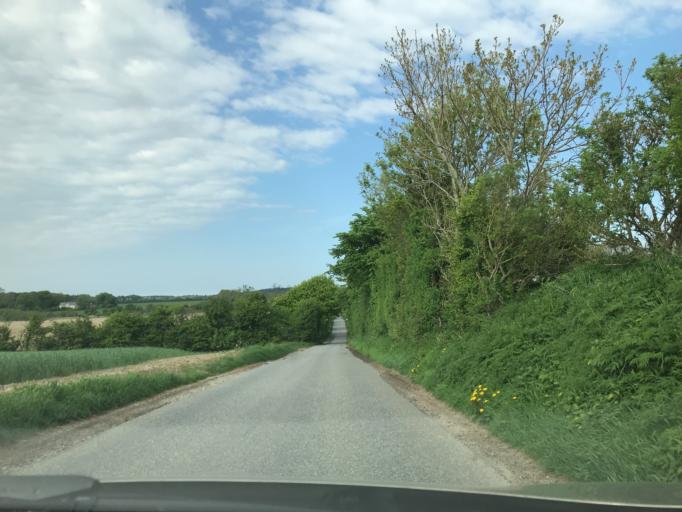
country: DK
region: South Denmark
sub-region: Middelfart Kommune
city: Norre Aby
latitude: 55.3892
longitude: 9.8544
